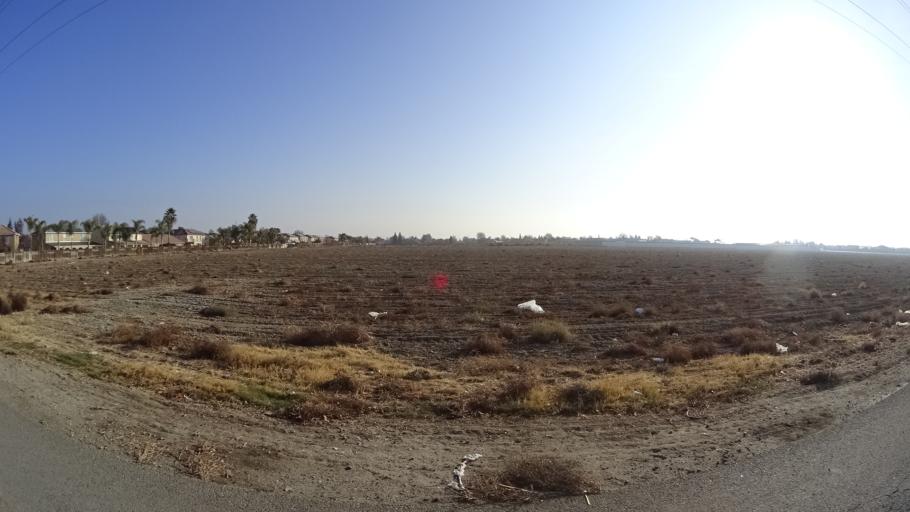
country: US
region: California
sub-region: Kern County
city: Greenacres
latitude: 35.2990
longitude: -119.1101
